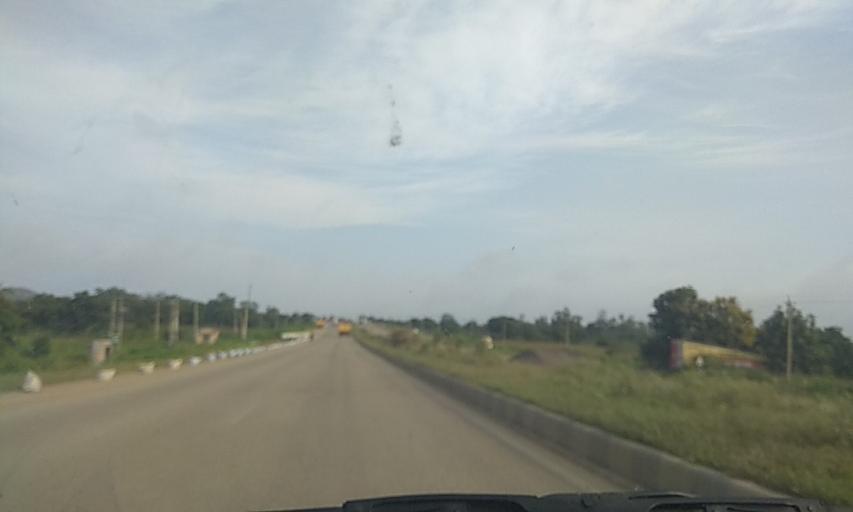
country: IN
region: Karnataka
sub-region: Haveri
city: Byadgi
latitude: 14.6982
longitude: 75.5255
